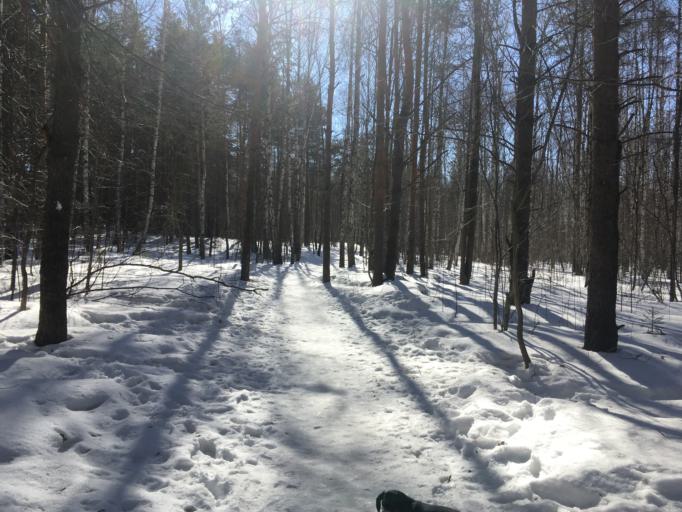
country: RU
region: Perm
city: Kondratovo
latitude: 57.9926
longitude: 56.1635
